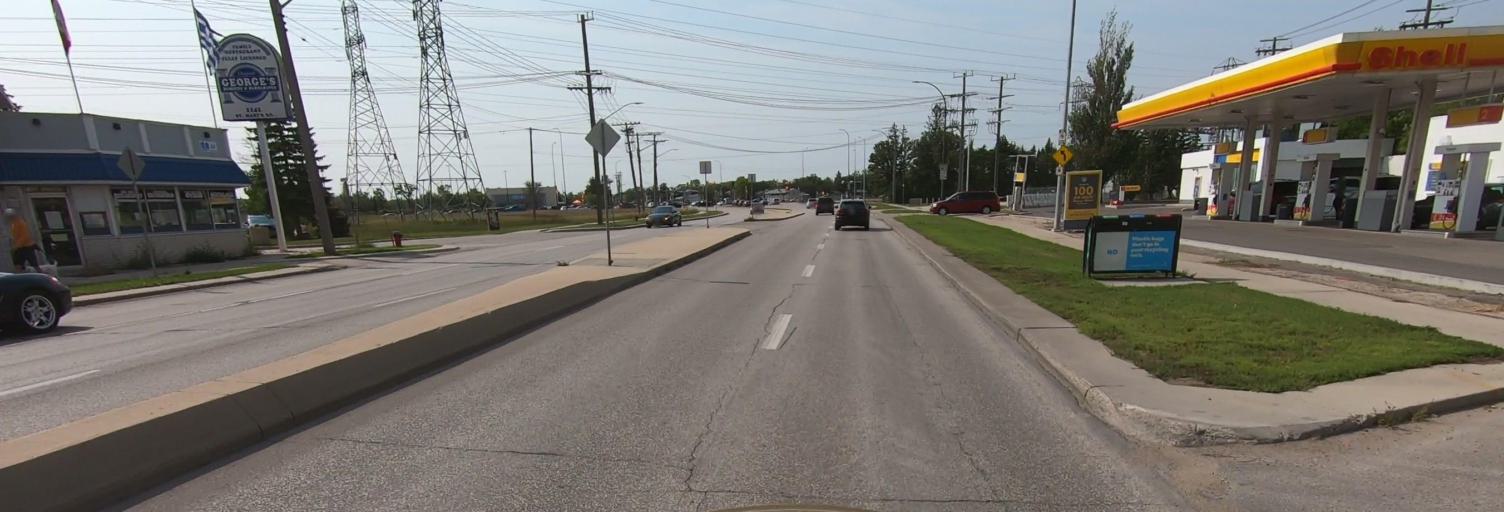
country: CA
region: Manitoba
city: Winnipeg
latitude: 49.8330
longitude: -97.1145
